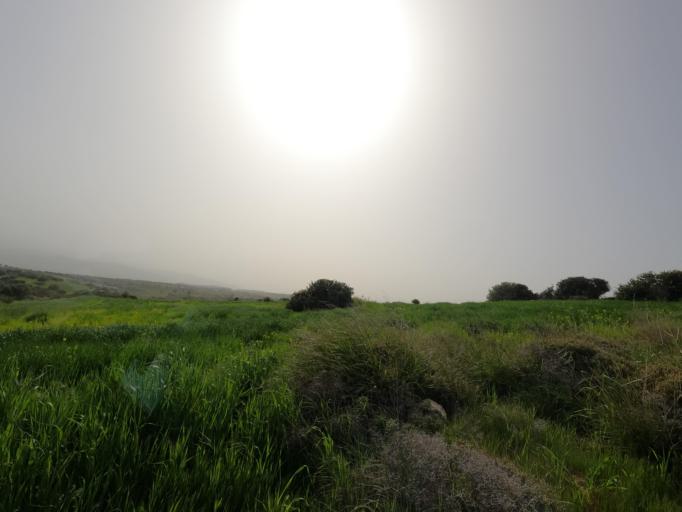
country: CY
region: Pafos
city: Polis
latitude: 35.0082
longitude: 32.3565
